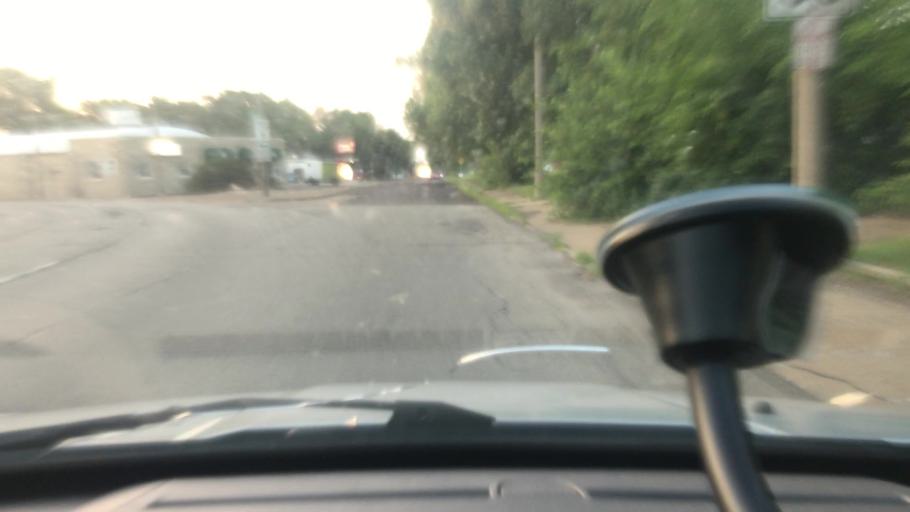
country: US
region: Illinois
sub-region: Tazewell County
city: Pekin
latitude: 40.5682
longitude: -89.6409
